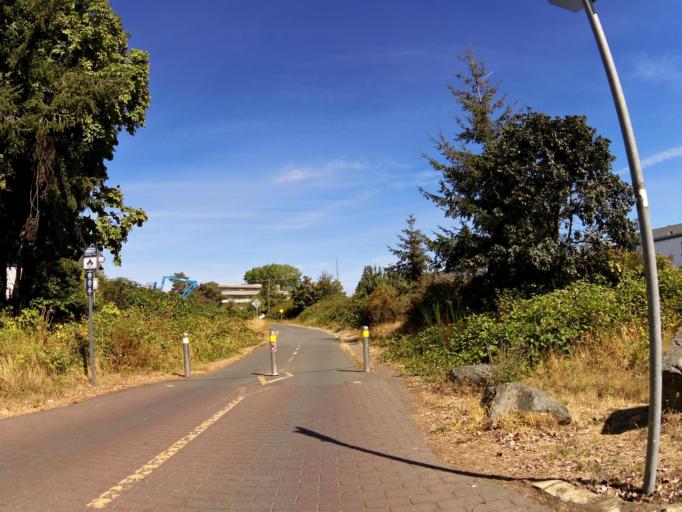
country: CA
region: British Columbia
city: Victoria
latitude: 48.4480
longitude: -123.3751
